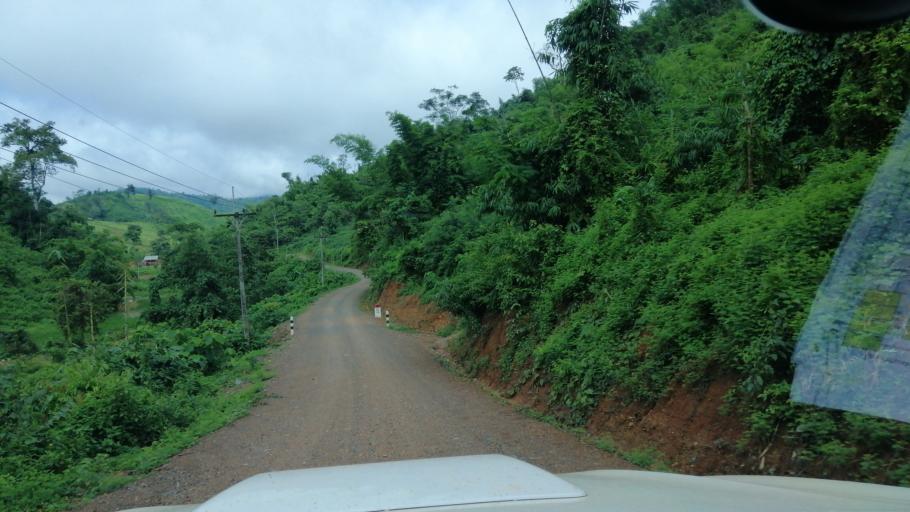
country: LA
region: Xiagnabouli
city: Muang Kenthao
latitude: 17.9171
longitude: 101.3661
